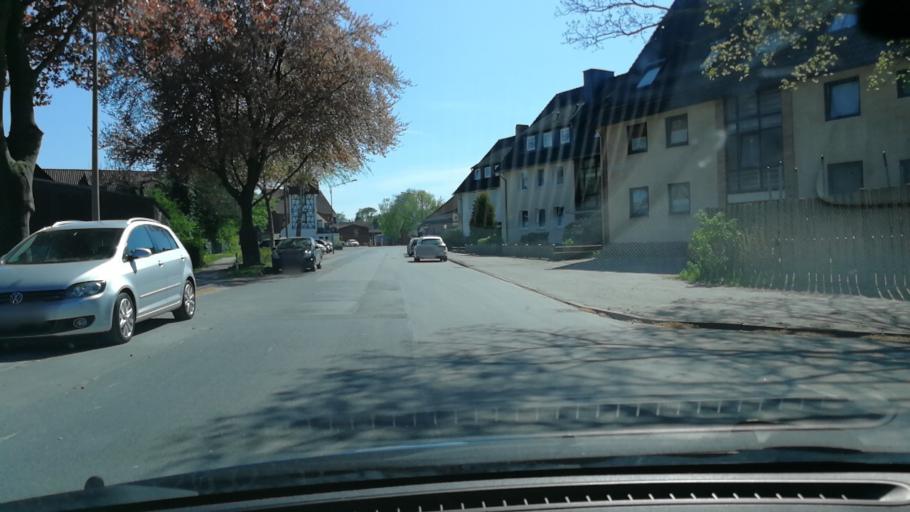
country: DE
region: Lower Saxony
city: Lehrte
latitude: 52.3657
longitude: 9.9120
